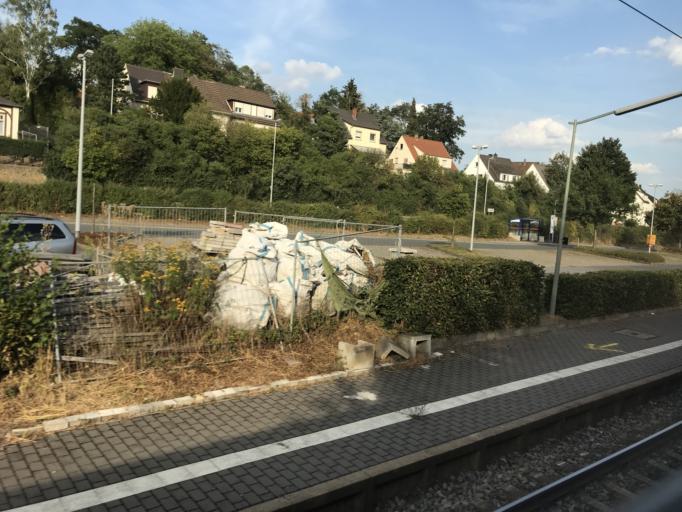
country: DE
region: Hesse
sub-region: Regierungsbezirk Giessen
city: Villmar
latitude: 50.3552
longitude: 8.1868
